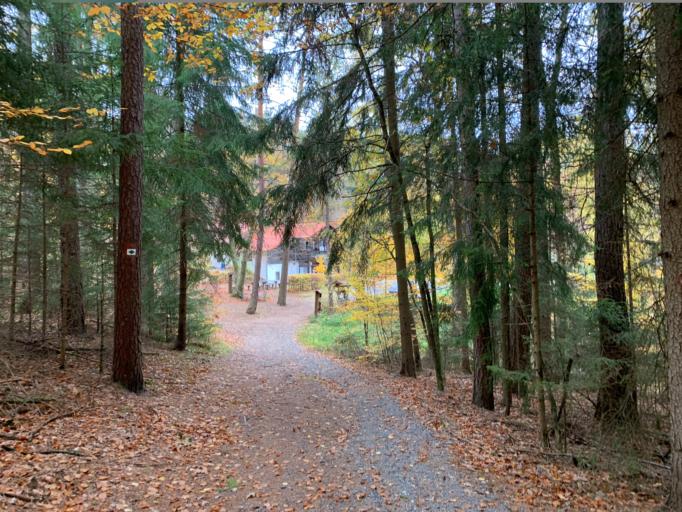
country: DE
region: Bavaria
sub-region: Upper Palatinate
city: Schnaittenbach
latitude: 49.5223
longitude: 12.0194
